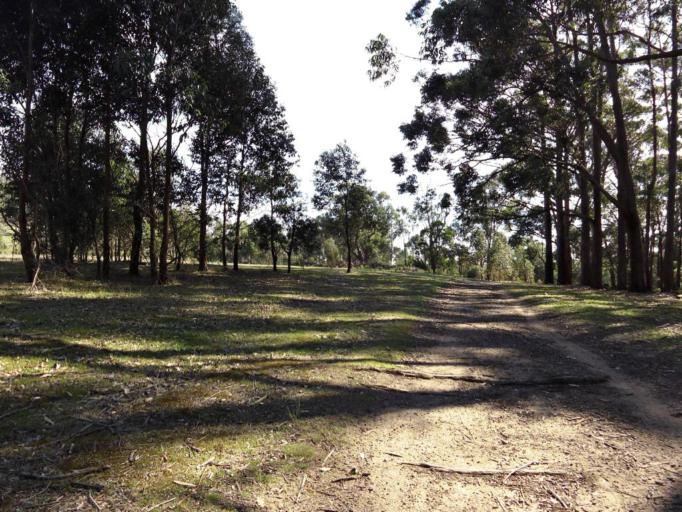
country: AU
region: Victoria
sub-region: Yarra Ranges
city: Lysterfield
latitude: -37.9412
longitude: 145.2745
